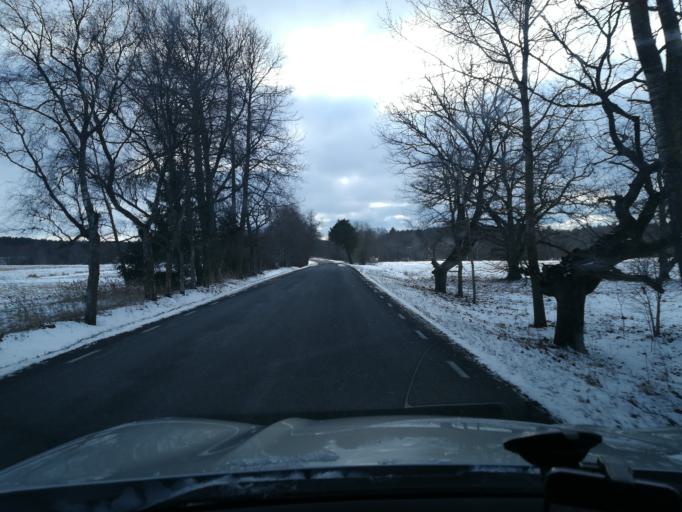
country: EE
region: Harju
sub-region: Keila linn
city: Keila
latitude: 59.4144
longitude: 24.4141
